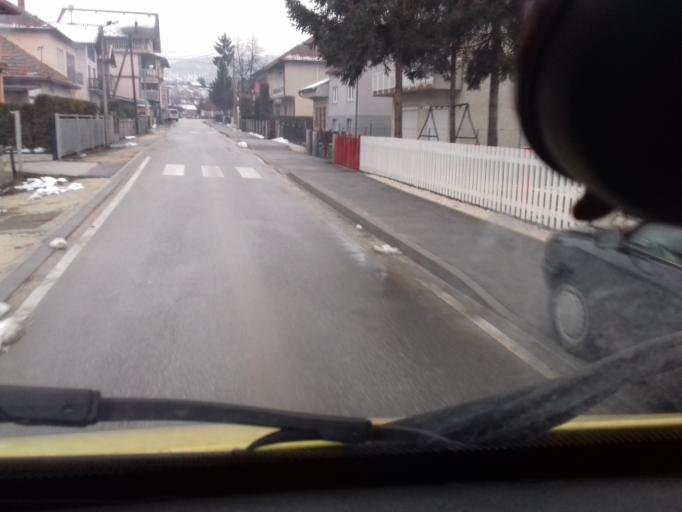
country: BA
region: Federation of Bosnia and Herzegovina
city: Vitez
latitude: 44.1564
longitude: 17.7865
